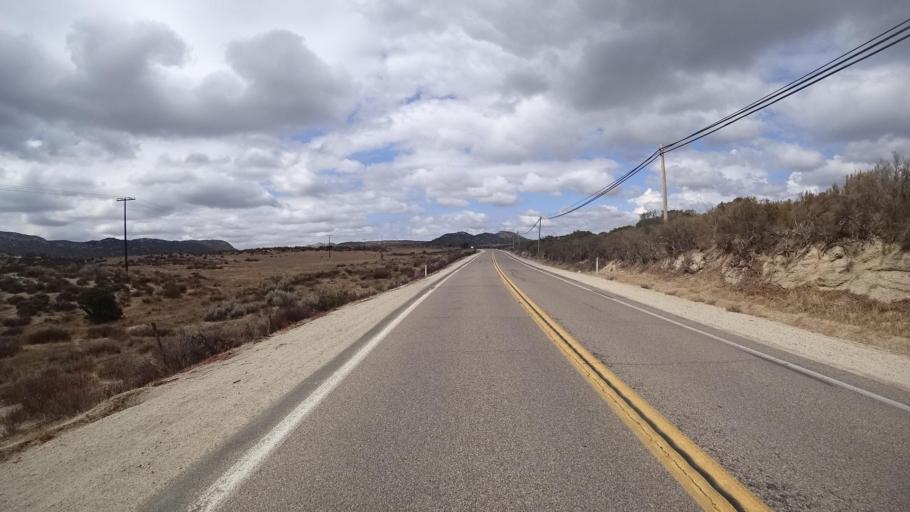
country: US
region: California
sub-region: San Diego County
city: Campo
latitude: 32.6359
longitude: -116.4781
